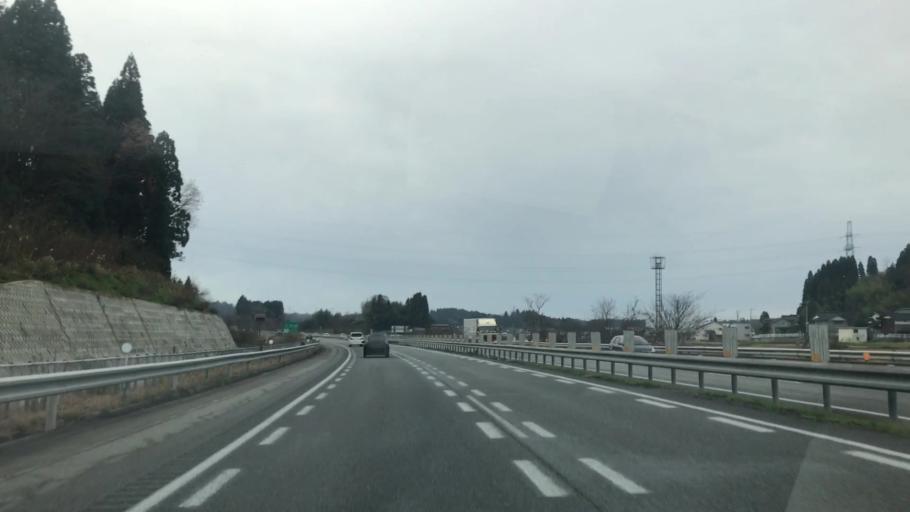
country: JP
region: Toyama
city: Kuragaki-kosugi
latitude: 36.6930
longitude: 137.0877
